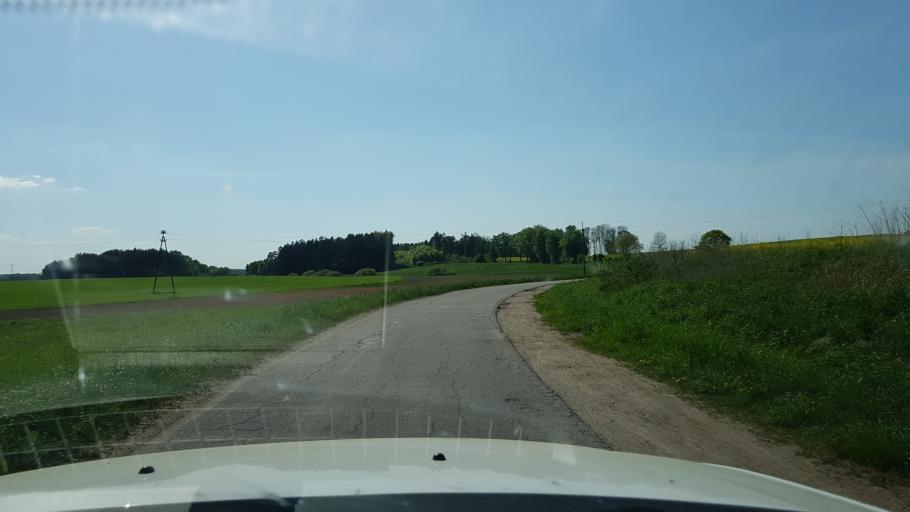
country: PL
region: West Pomeranian Voivodeship
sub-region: Powiat kolobrzeski
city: Ryman
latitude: 53.9933
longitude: 15.5377
